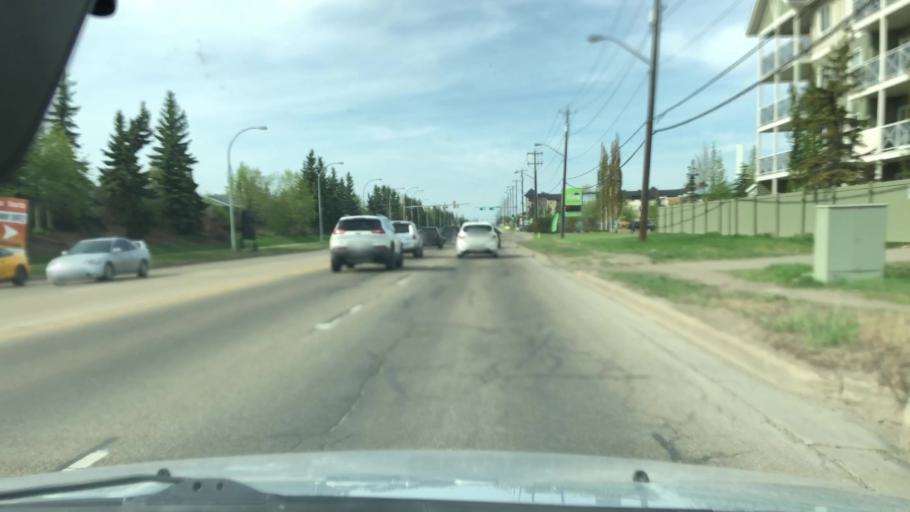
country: CA
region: Alberta
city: Edmonton
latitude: 53.6048
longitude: -113.5412
